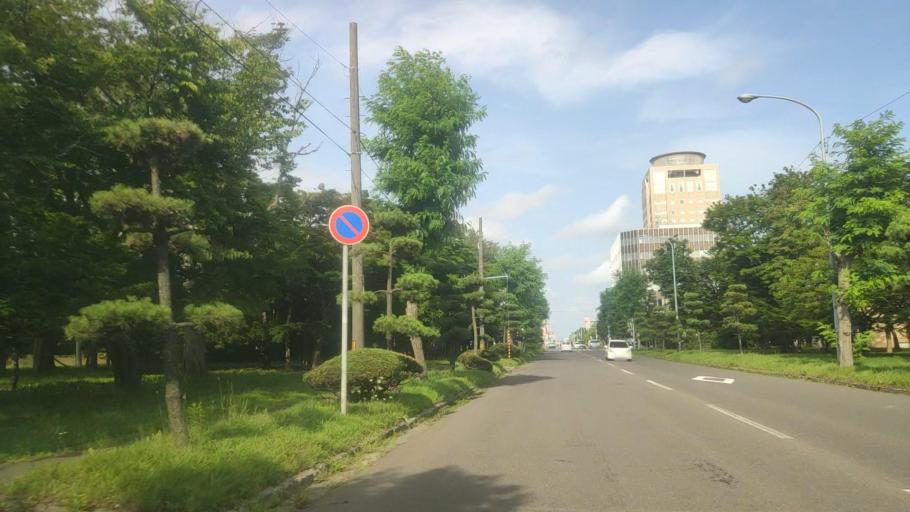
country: JP
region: Hokkaido
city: Tomakomai
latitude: 42.6366
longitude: 141.5962
